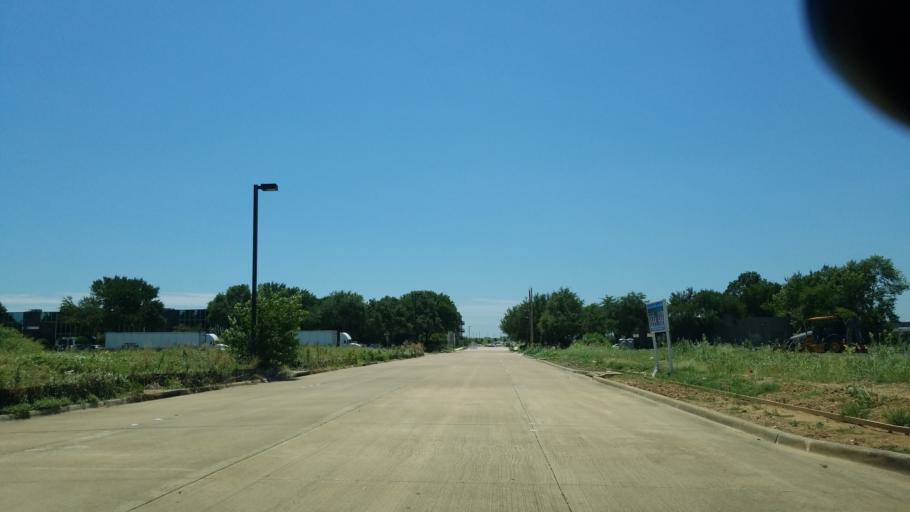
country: US
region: Texas
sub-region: Dallas County
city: Farmers Branch
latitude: 32.9206
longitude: -96.9121
